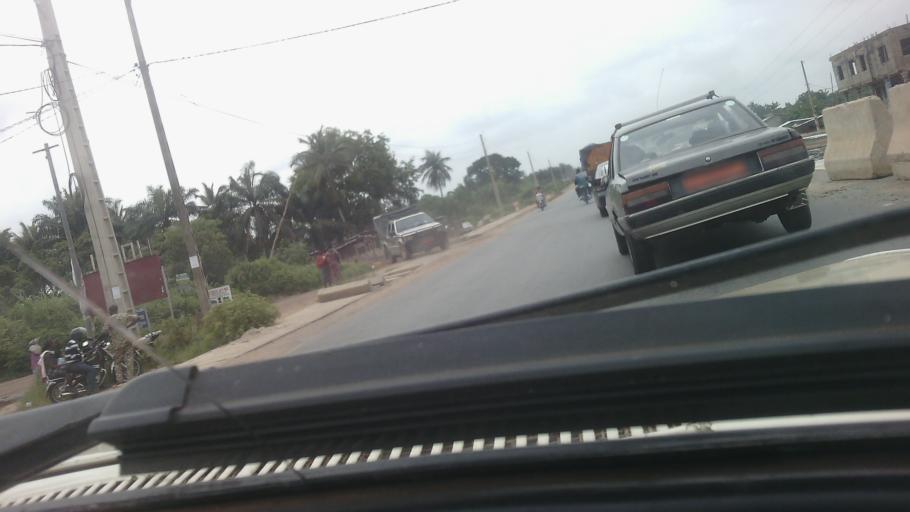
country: BJ
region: Atlantique
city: Hevie
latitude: 6.3827
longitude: 2.1799
